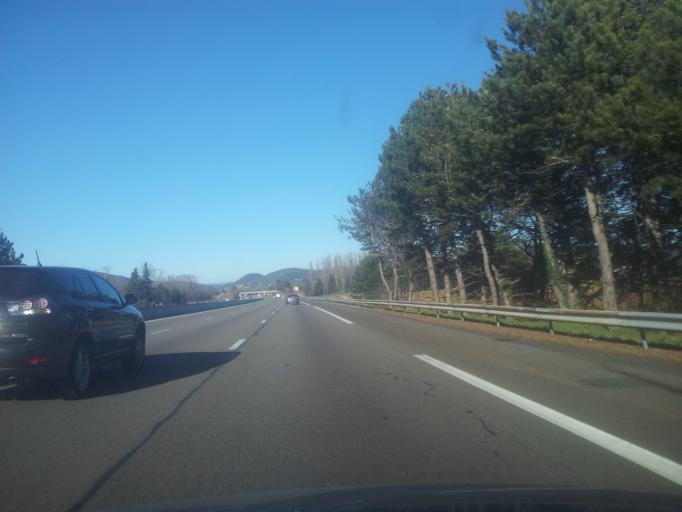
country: FR
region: Rhone-Alpes
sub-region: Departement de la Drome
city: Montboucher-sur-Jabron
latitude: 44.5644
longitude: 4.8109
